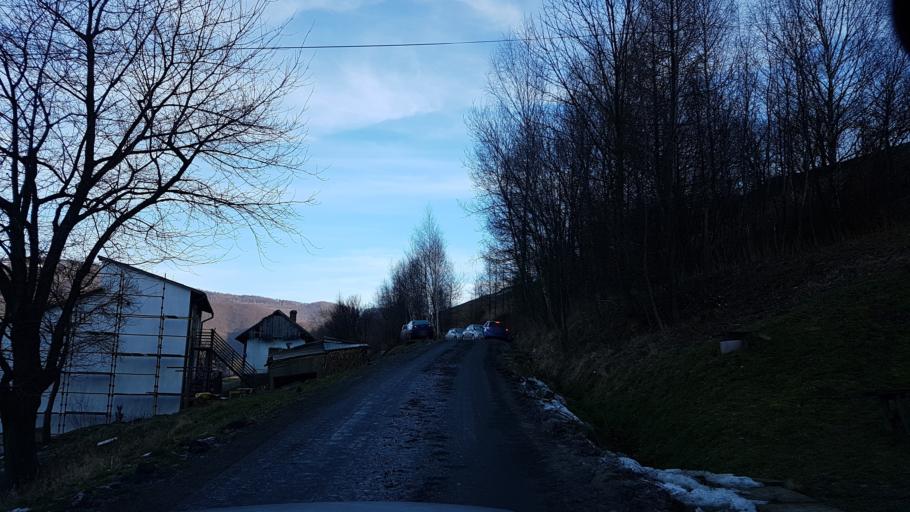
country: PL
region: Lesser Poland Voivodeship
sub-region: Powiat nowosadecki
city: Rytro
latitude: 49.4956
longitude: 20.6667
